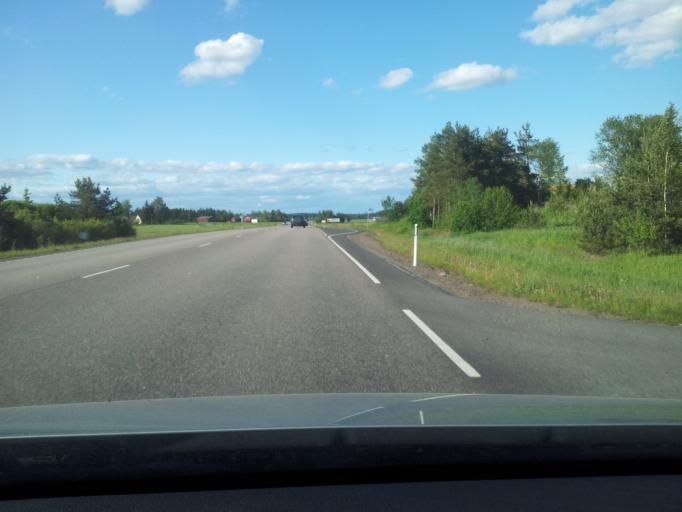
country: FI
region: Kymenlaakso
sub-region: Kouvola
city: Elimaeki
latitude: 60.7530
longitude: 26.4586
